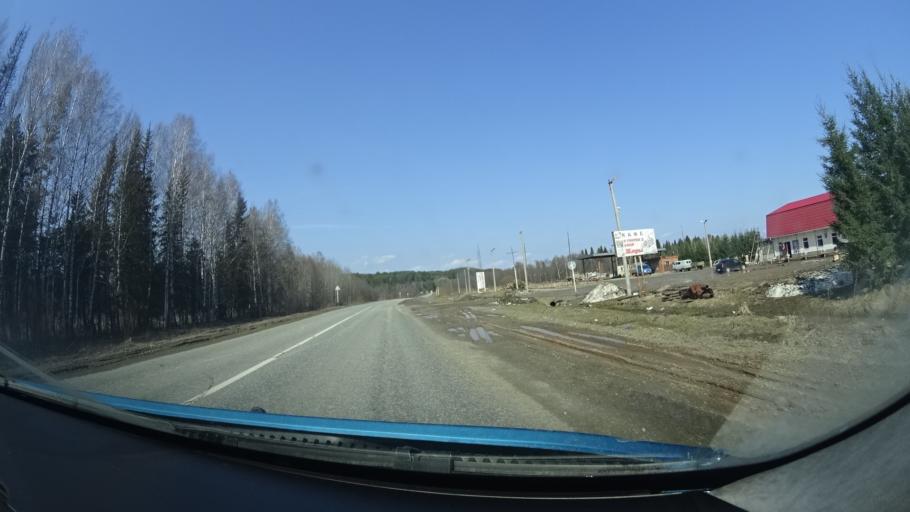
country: RU
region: Perm
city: Yugo-Kamskiy
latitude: 57.5400
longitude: 55.6864
